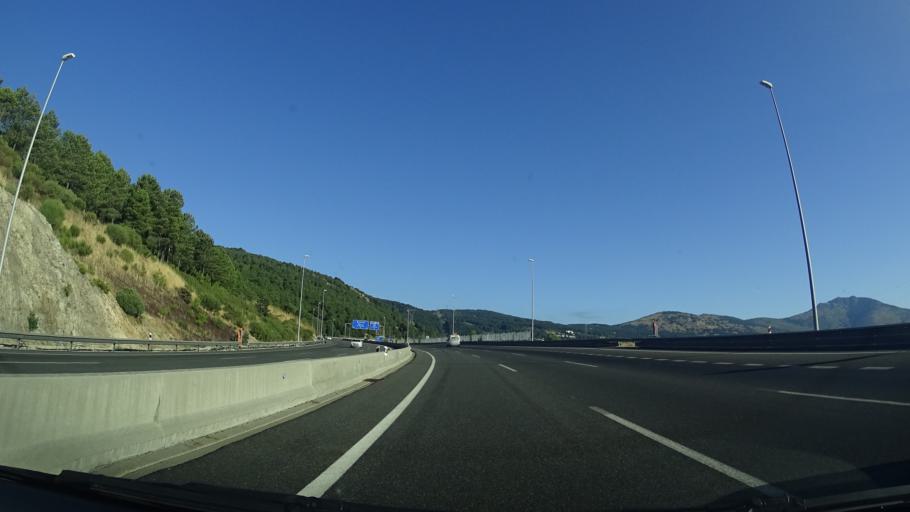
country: ES
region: Madrid
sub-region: Provincia de Madrid
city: Guadarrama
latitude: 40.6858
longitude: -4.1180
